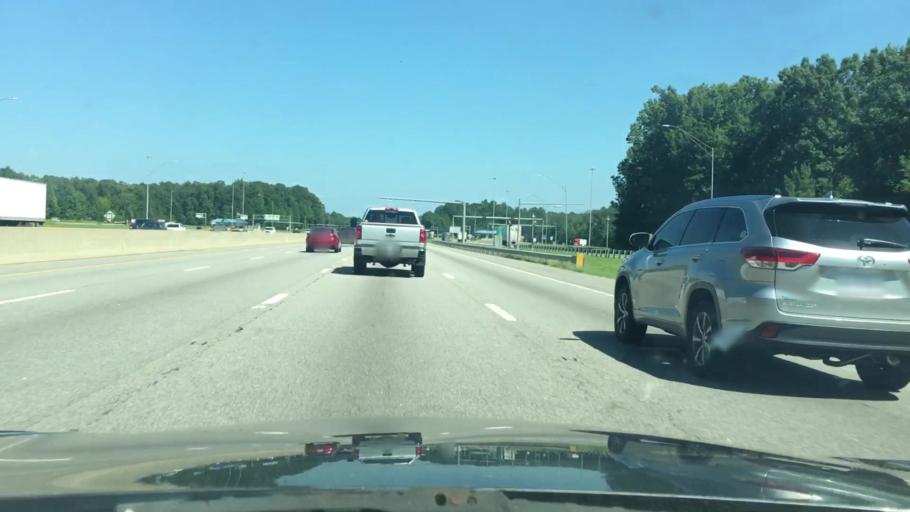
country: US
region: North Carolina
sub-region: Alamance County
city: Mebane
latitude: 36.0783
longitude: -79.2124
